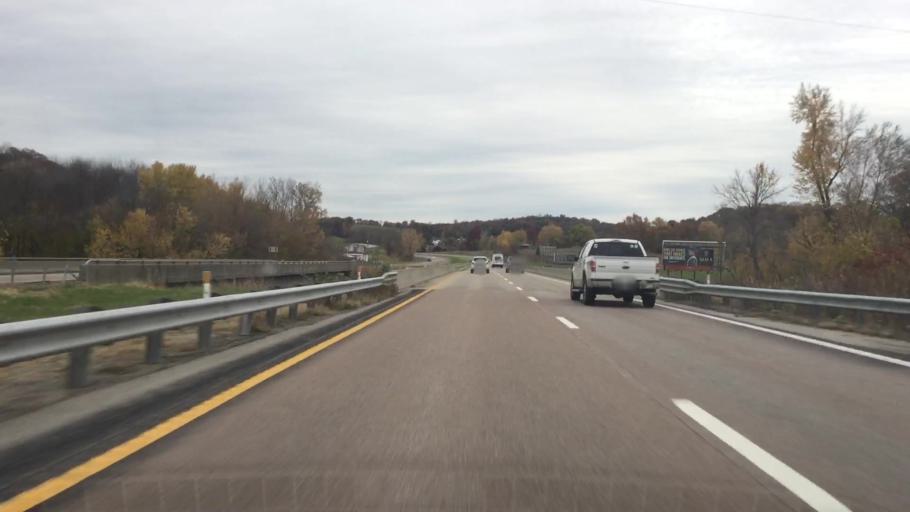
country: US
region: Missouri
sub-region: Cole County
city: Jefferson City
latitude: 38.6447
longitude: -92.2011
